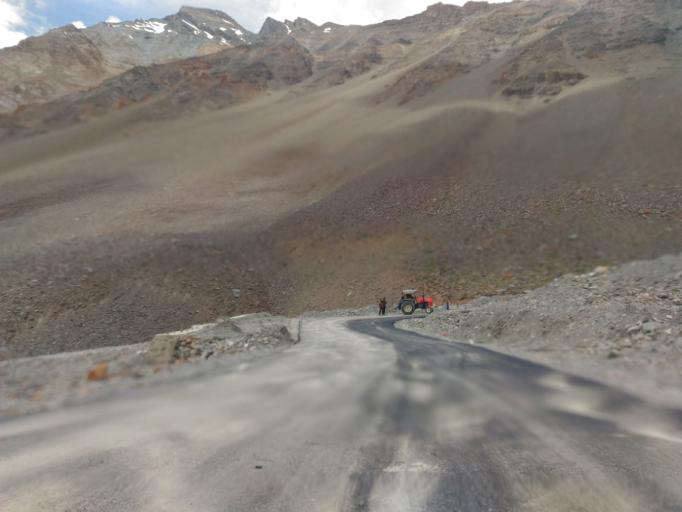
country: IN
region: Himachal Pradesh
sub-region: Lahul and Spiti
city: Kyelang
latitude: 32.7852
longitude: 77.3547
